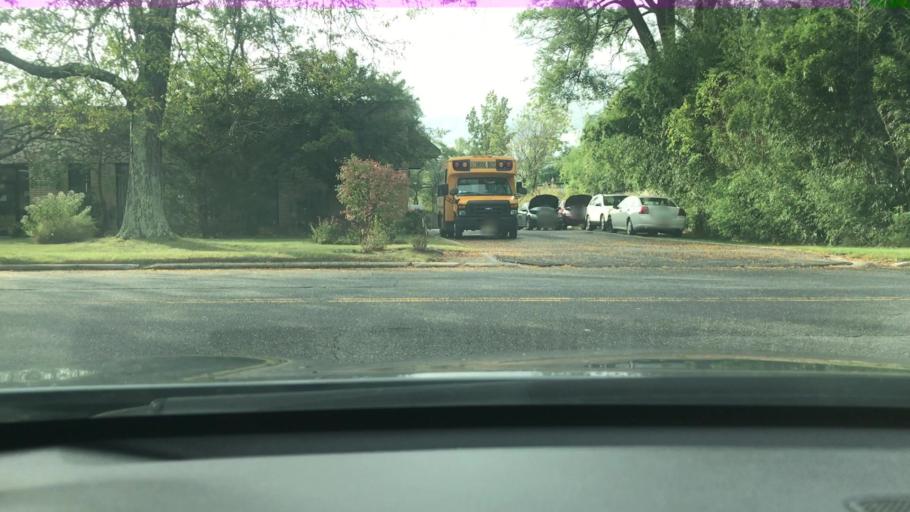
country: US
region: New York
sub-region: Nassau County
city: Woodbury
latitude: 40.8084
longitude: -73.4838
